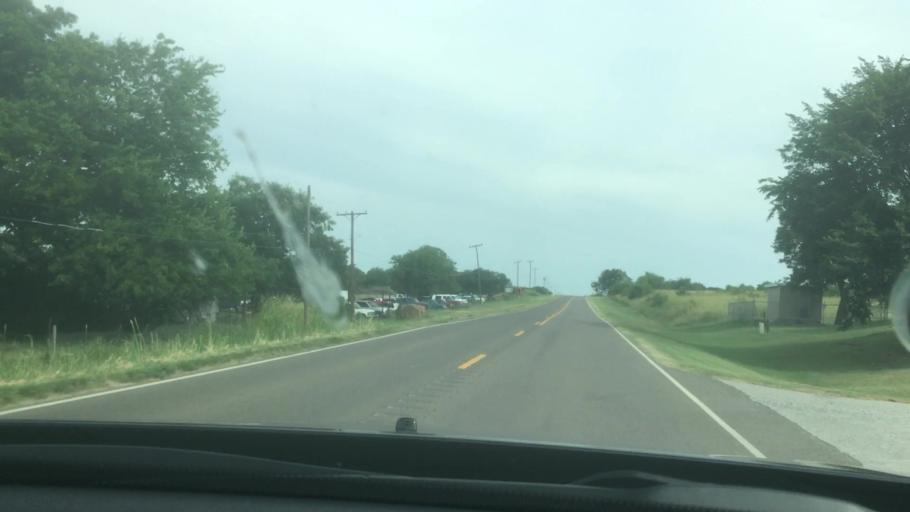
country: US
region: Oklahoma
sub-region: Garvin County
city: Pauls Valley
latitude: 34.7440
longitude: -97.2808
